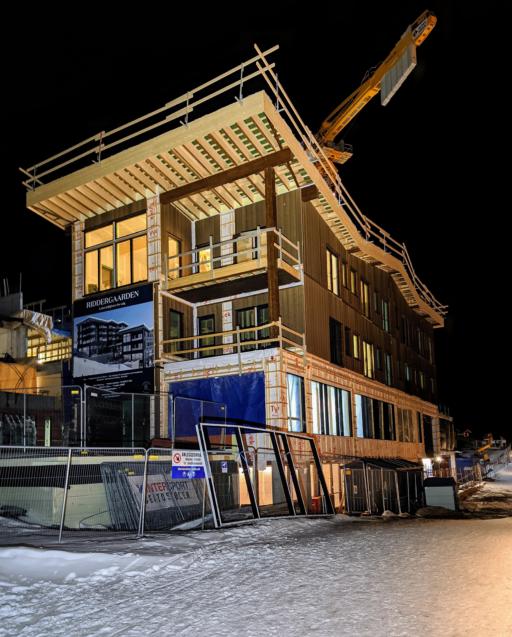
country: NO
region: Oppland
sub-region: Vestre Slidre
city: Slidre
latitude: 61.2495
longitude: 8.9055
